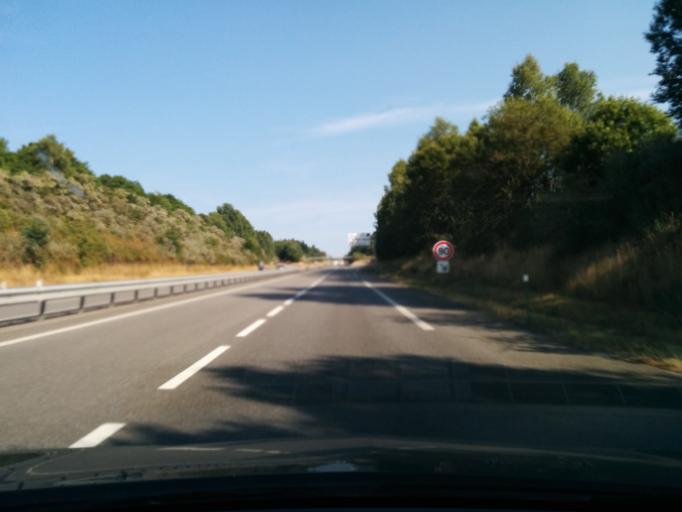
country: FR
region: Limousin
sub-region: Departement de la Haute-Vienne
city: Saint-Germain-les-Belles
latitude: 45.5875
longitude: 1.4691
